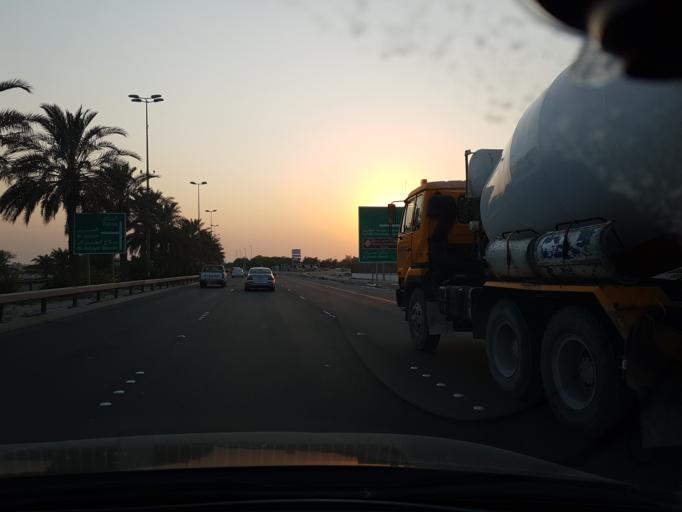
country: BH
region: Central Governorate
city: Dar Kulayb
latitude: 26.0577
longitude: 50.5045
